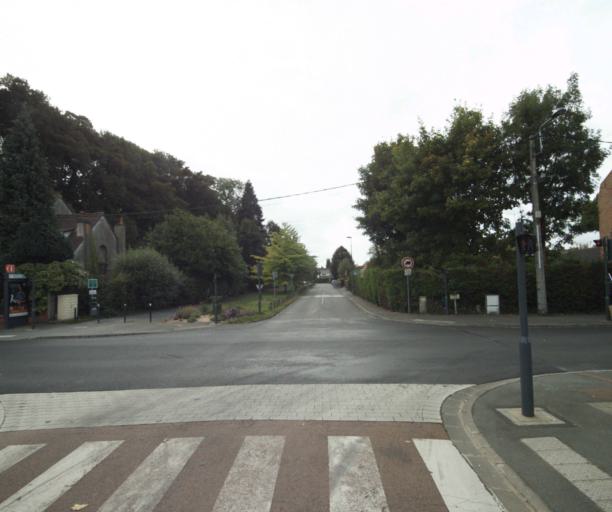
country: FR
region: Nord-Pas-de-Calais
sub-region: Departement du Nord
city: Lambersart
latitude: 50.6646
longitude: 3.0317
